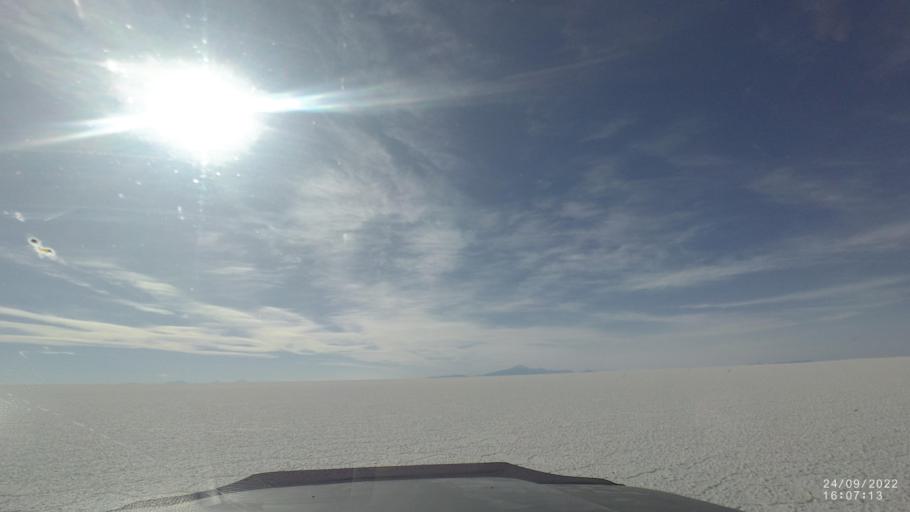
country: BO
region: Potosi
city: Colchani
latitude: -20.3011
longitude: -67.3005
